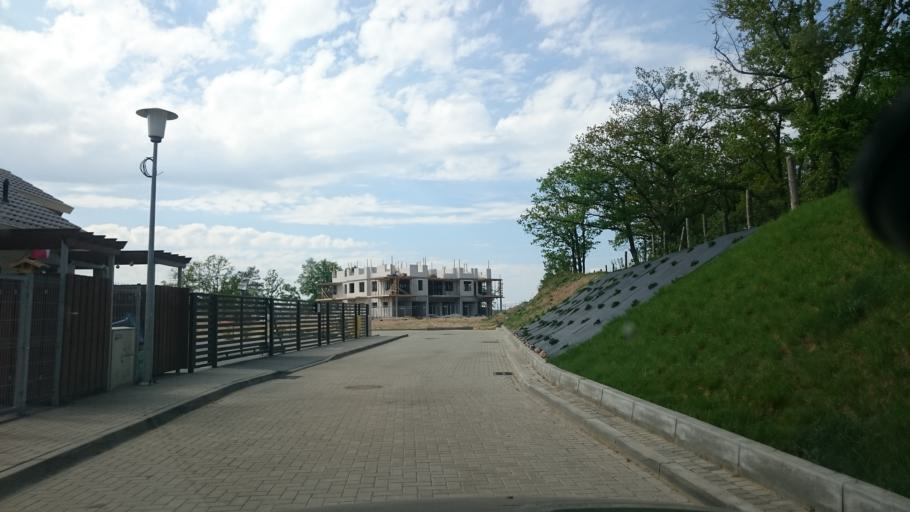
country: PL
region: Kujawsko-Pomorskie
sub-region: Grudziadz
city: Grudziadz
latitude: 53.4482
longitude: 18.7118
